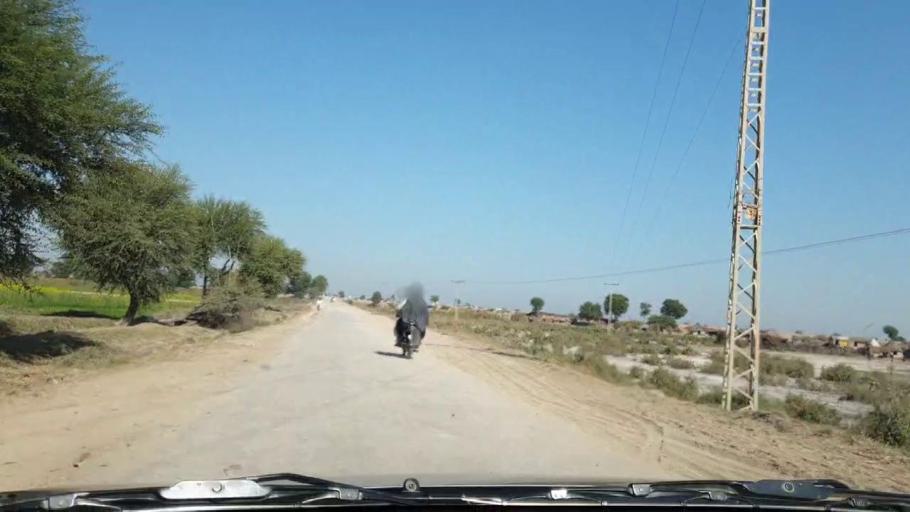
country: PK
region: Sindh
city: Sinjhoro
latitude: 26.1151
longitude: 68.8193
